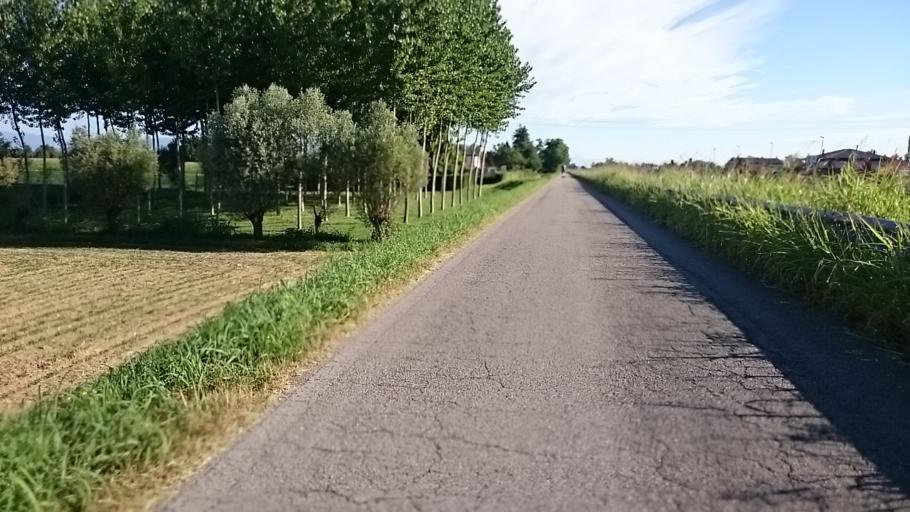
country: IT
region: Veneto
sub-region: Provincia di Padova
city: Campodarsego
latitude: 45.5139
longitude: 11.9109
